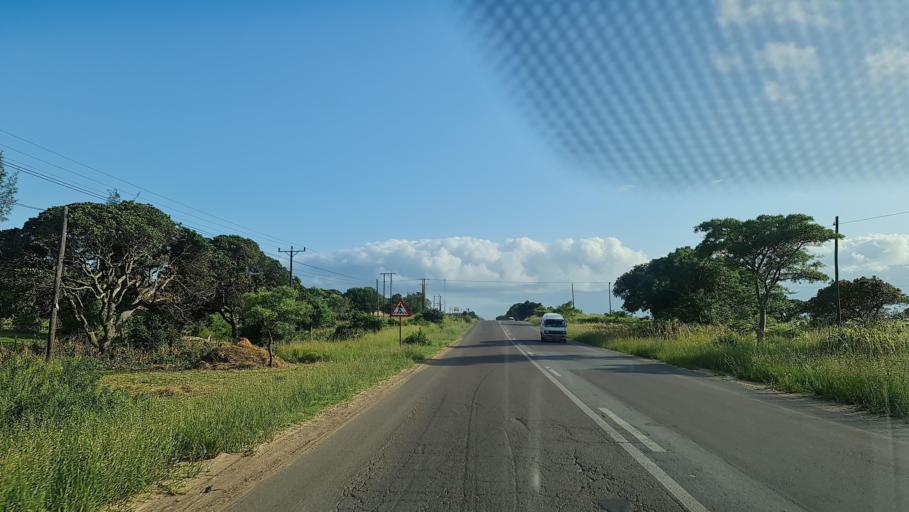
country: MZ
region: Maputo City
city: Maputo
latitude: -25.6773
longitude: 32.6672
